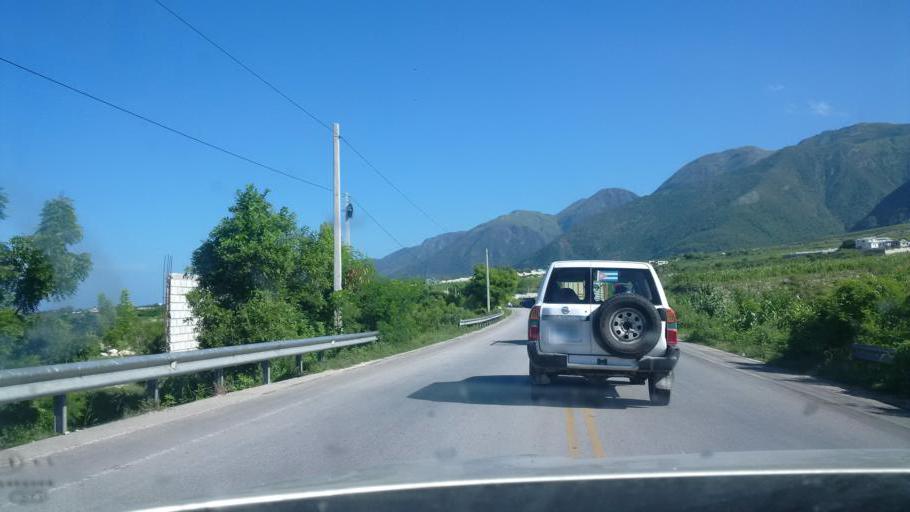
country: HT
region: Ouest
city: Cabaret
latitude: 18.8562
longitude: -72.5926
